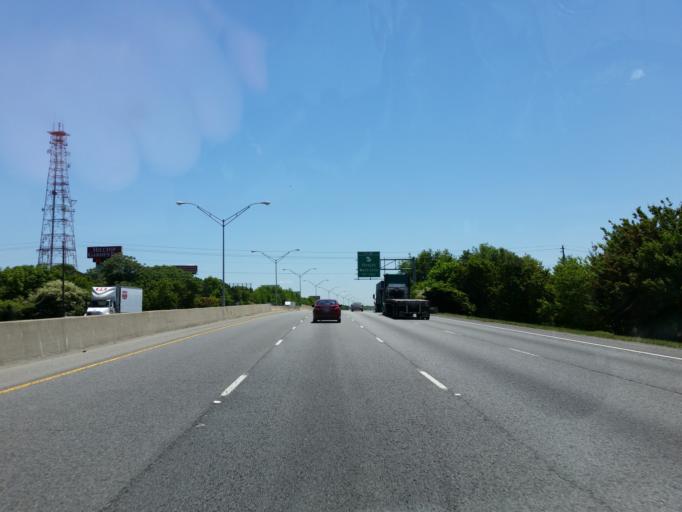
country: US
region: Georgia
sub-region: Monroe County
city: Forsyth
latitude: 33.0546
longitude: -83.9525
